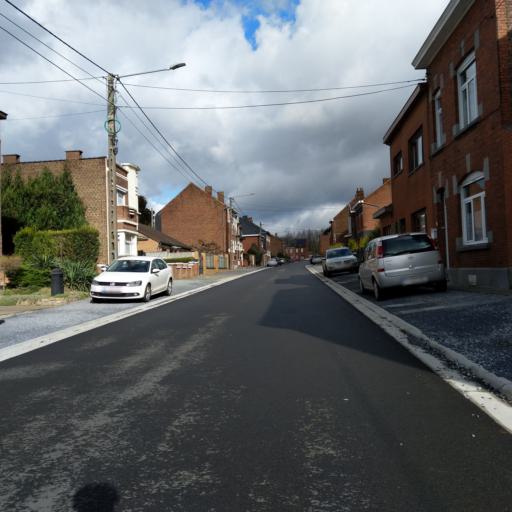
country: BE
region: Wallonia
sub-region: Province du Hainaut
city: Mons
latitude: 50.4782
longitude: 3.9448
